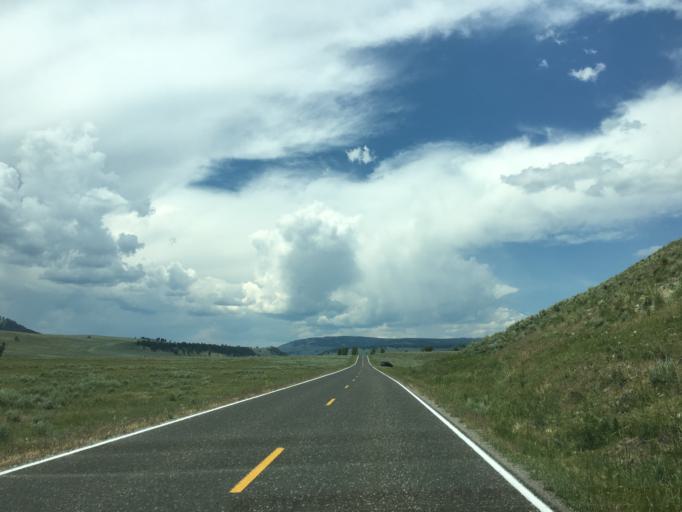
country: US
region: Montana
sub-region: Park County
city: Livingston
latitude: 44.8899
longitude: -110.2271
